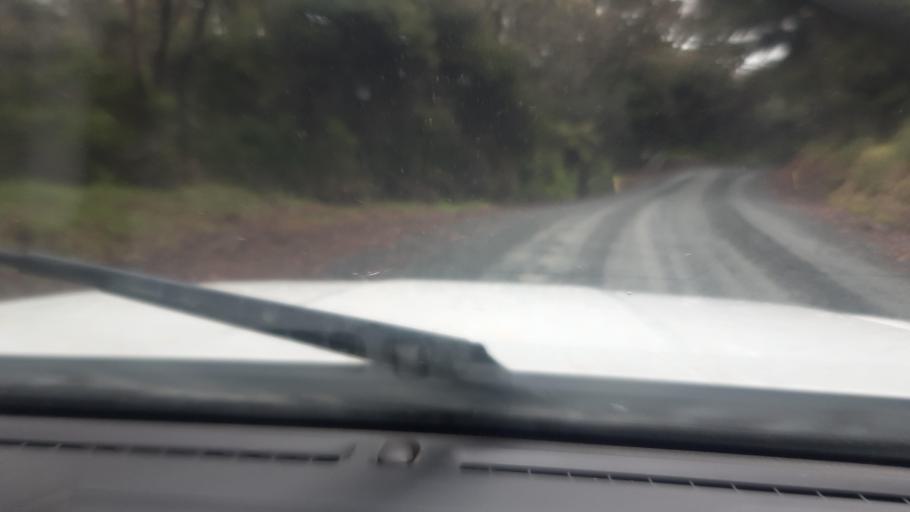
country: NZ
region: Northland
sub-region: Far North District
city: Kaitaia
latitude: -35.0033
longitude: 173.2160
